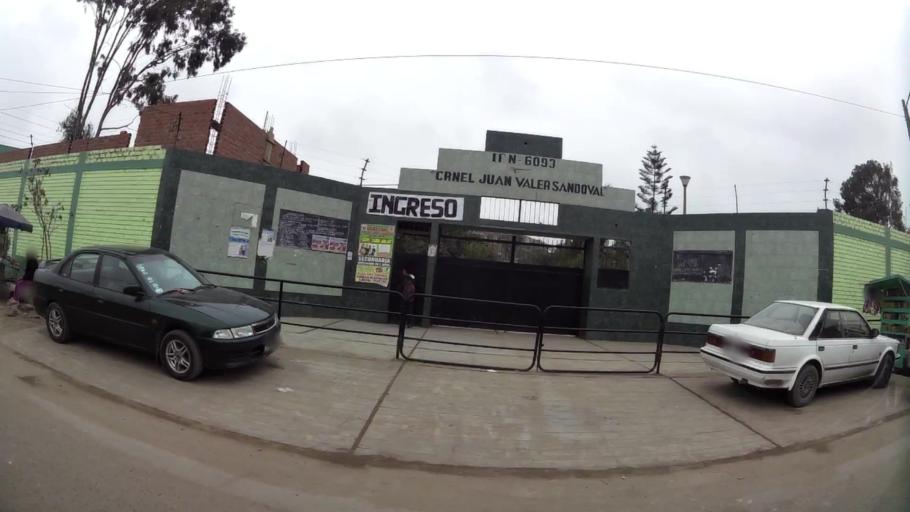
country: PE
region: Lima
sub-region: Lima
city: Cieneguilla
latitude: -12.2281
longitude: -76.9080
